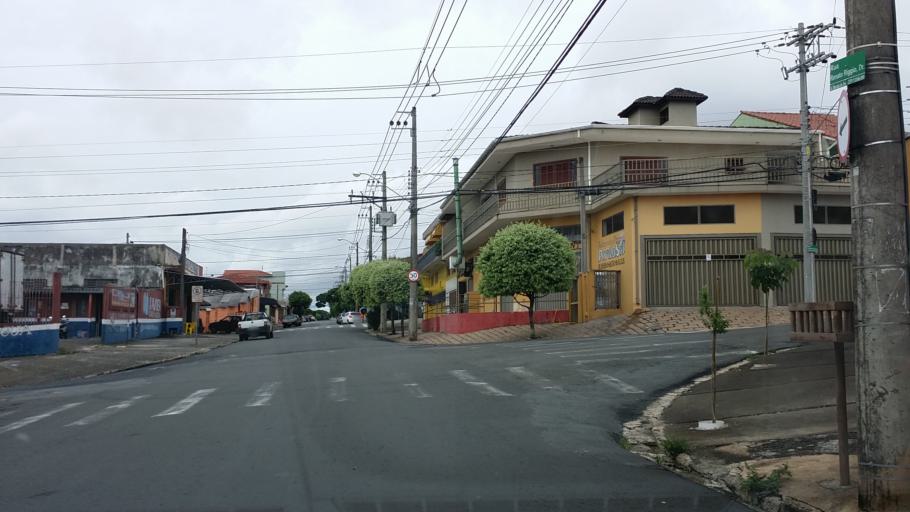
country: BR
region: Sao Paulo
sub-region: Indaiatuba
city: Indaiatuba
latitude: -23.1241
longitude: -47.2305
